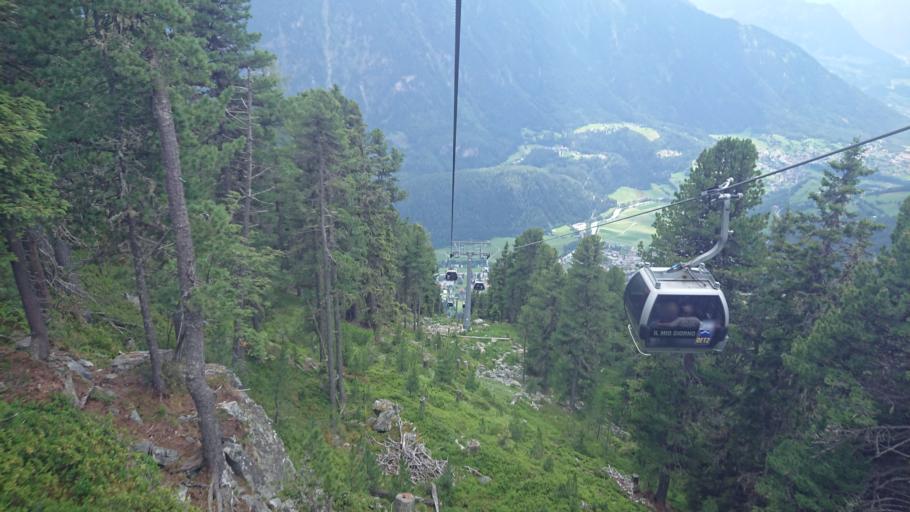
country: AT
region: Tyrol
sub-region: Politischer Bezirk Imst
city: Oetz
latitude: 47.2105
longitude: 10.9283
